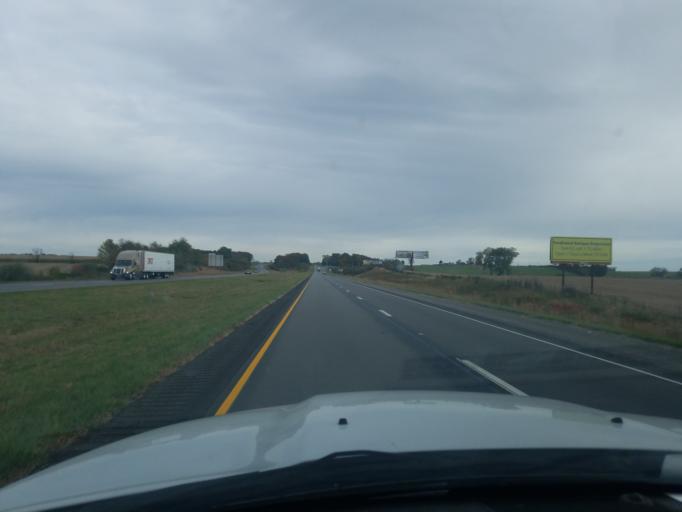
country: US
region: Indiana
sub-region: Spencer County
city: Dale
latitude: 38.1944
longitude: -86.9642
